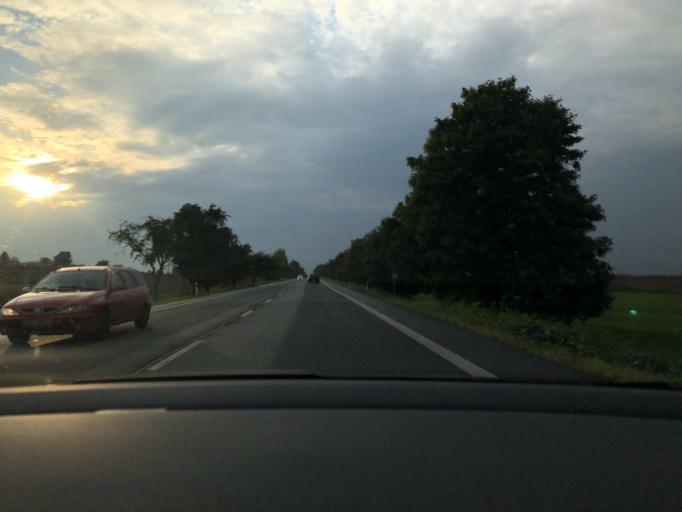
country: CZ
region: Central Bohemia
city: Velim
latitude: 50.0369
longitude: 15.1376
